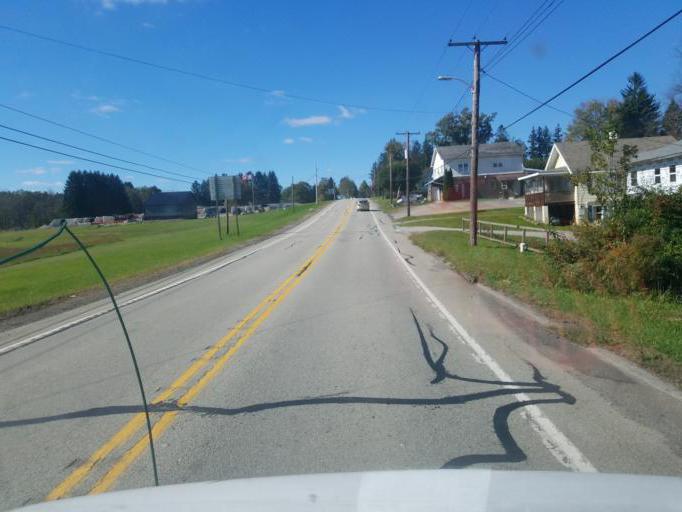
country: US
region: Pennsylvania
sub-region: Somerset County
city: Boswell
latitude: 40.1629
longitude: -79.0764
